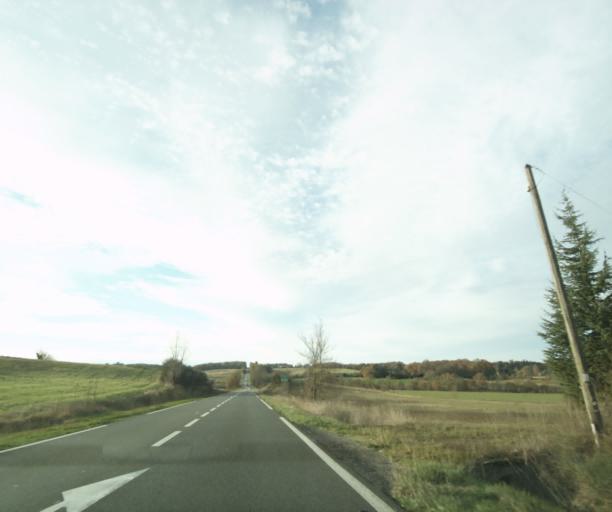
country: FR
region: Midi-Pyrenees
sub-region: Departement du Gers
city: Vic-Fezensac
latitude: 43.7514
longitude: 0.2683
